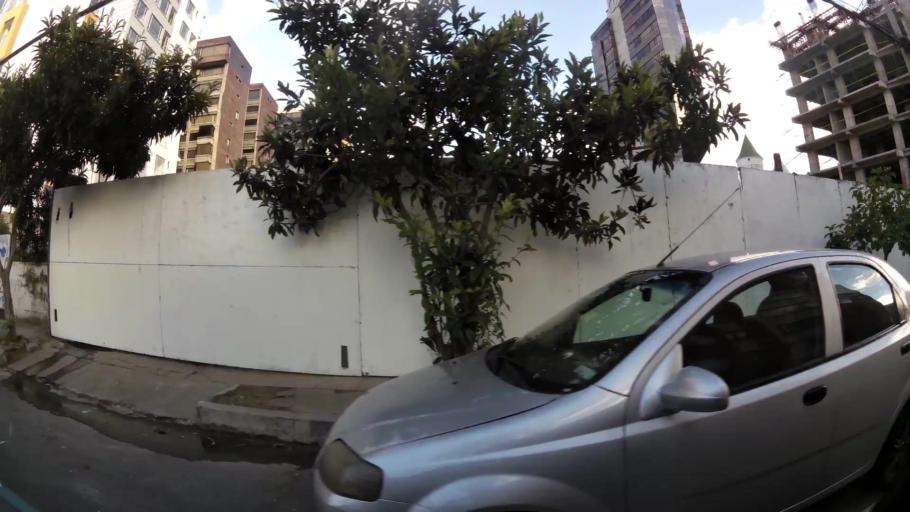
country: EC
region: Pichincha
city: Quito
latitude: -0.2048
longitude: -78.4870
